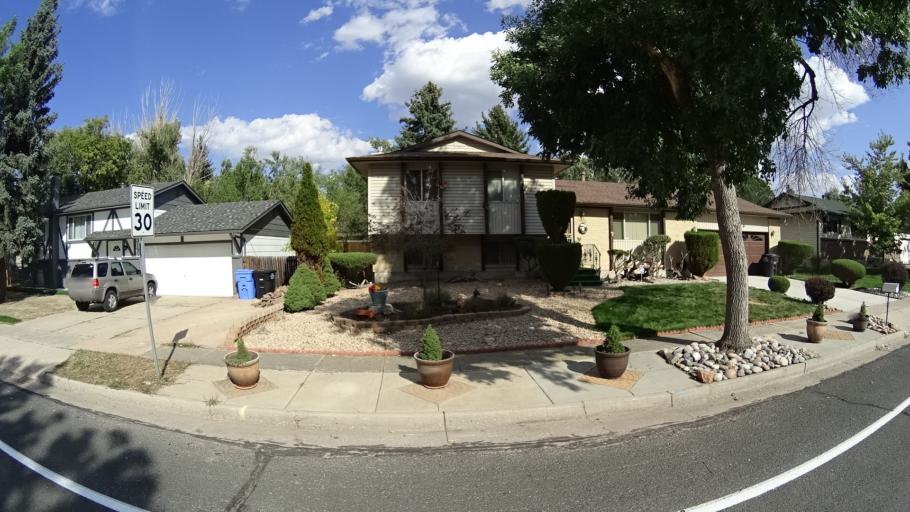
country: US
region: Colorado
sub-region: El Paso County
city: Cimarron Hills
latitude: 38.8776
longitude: -104.7399
